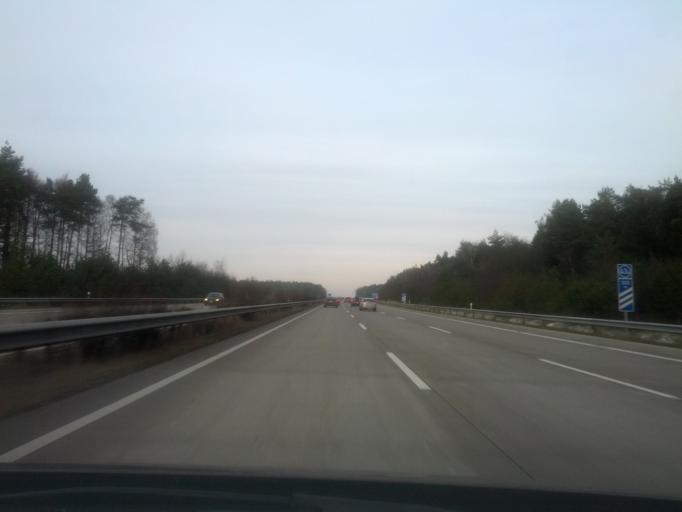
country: DE
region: Lower Saxony
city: Bispingen
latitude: 53.0743
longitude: 9.9594
